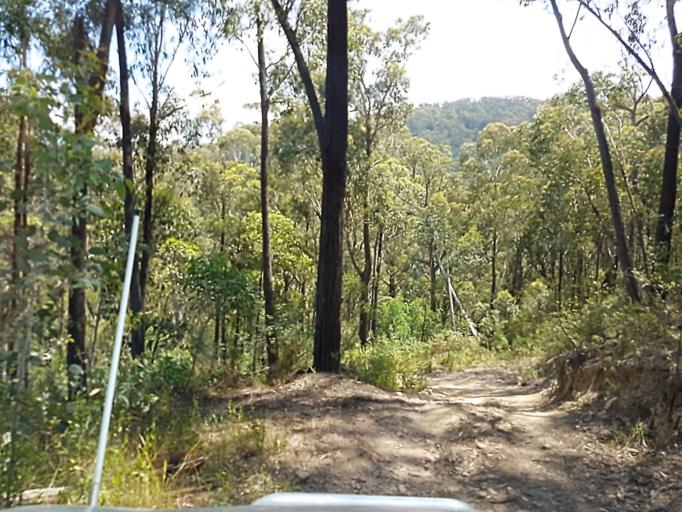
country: AU
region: Victoria
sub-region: East Gippsland
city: Lakes Entrance
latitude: -37.4031
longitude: 148.2990
